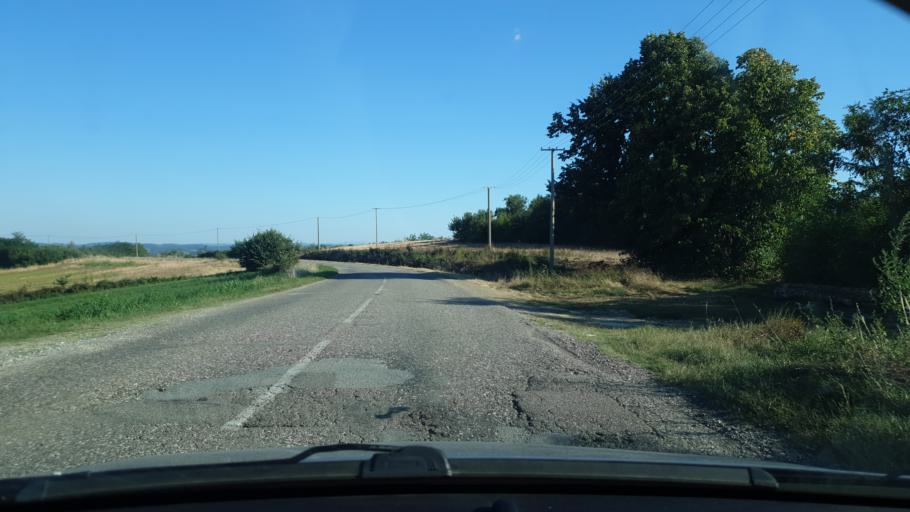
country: RS
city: Rumska
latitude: 44.5876
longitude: 19.5689
